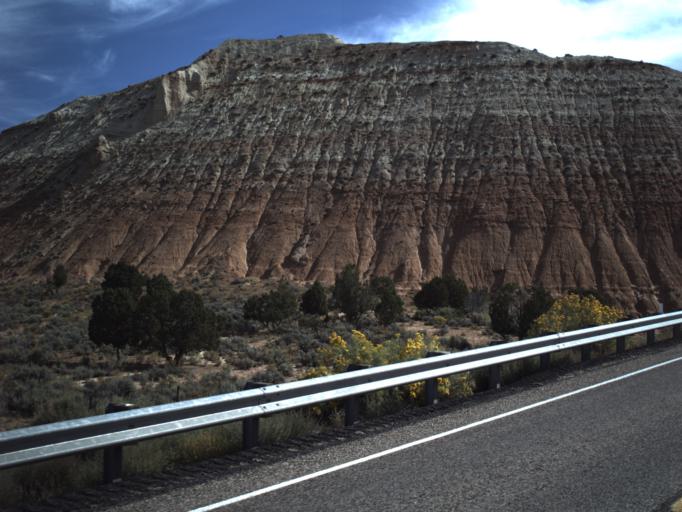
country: US
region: Utah
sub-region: Garfield County
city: Panguitch
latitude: 37.5644
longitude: -112.0411
